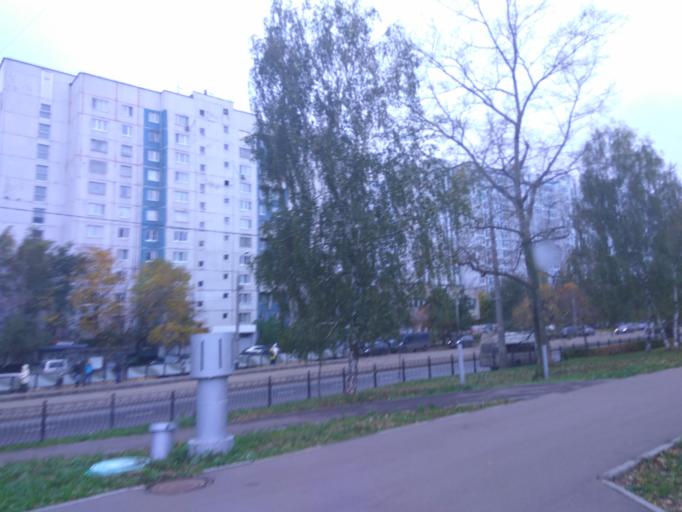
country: RU
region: Moscow
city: Strogino
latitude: 55.7995
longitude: 37.4015
